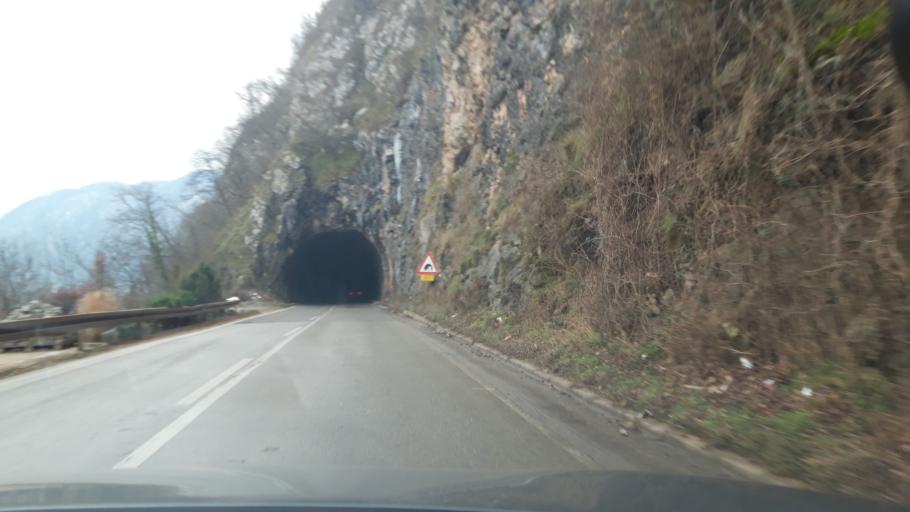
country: RS
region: Central Serbia
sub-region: Macvanski Okrug
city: Mali Zvornik
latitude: 44.3474
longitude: 19.1115
